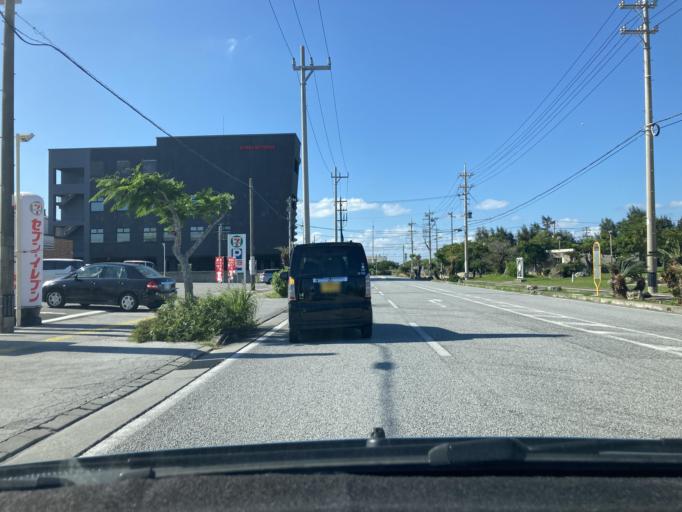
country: JP
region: Okinawa
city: Naha-shi
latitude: 26.2453
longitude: 127.6881
